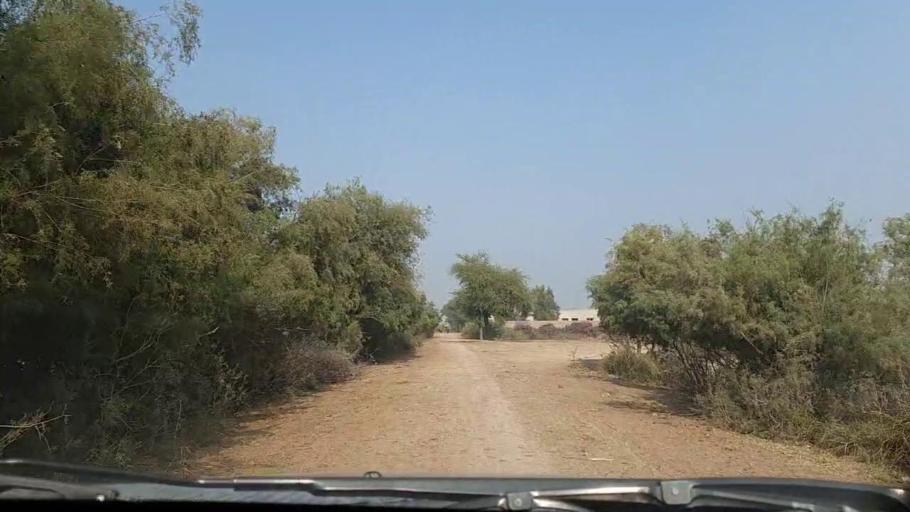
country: PK
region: Sindh
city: Sanghar
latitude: 26.0758
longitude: 68.9503
